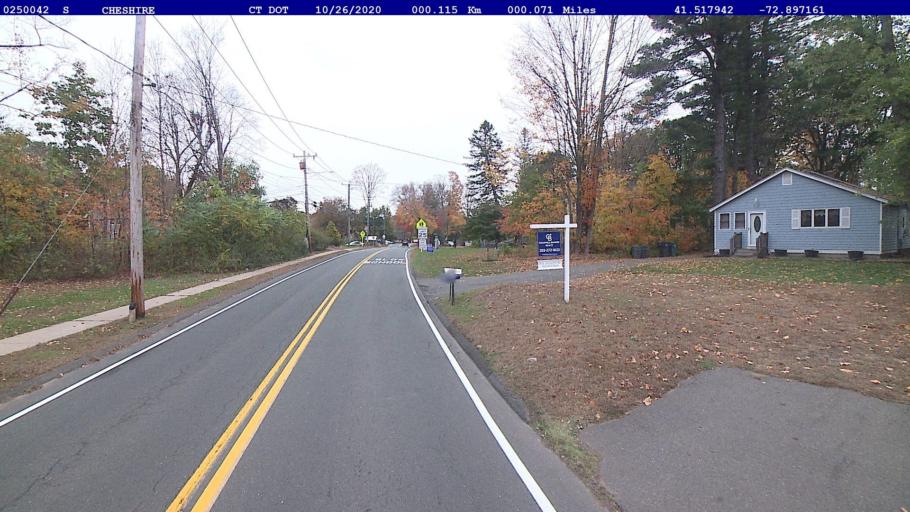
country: US
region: Connecticut
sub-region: New Haven County
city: Cheshire Village
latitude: 41.5180
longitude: -72.8972
